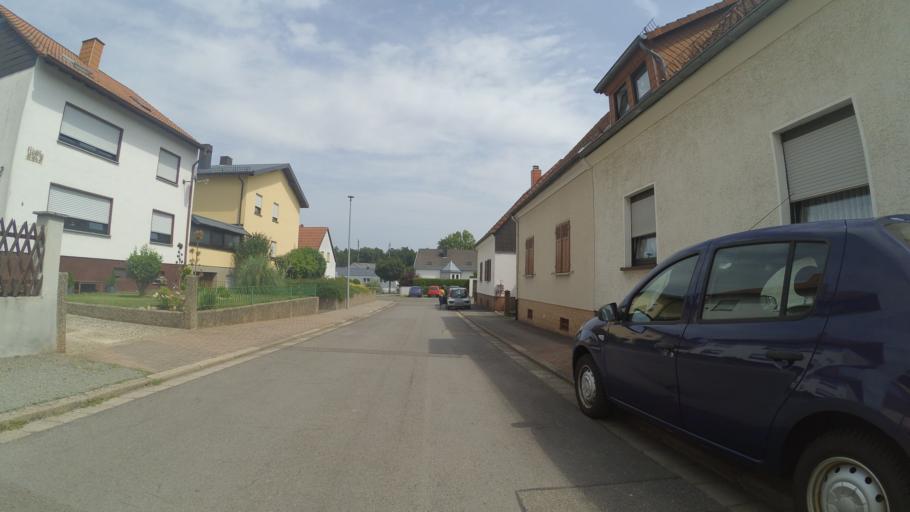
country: DE
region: Rheinland-Pfalz
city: Waldmohr
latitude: 49.3661
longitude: 7.3219
